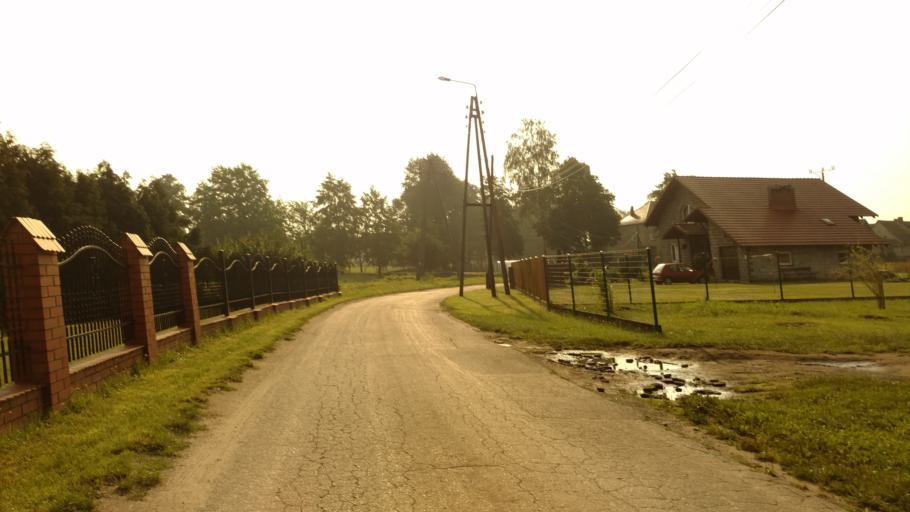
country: PL
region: Silesian Voivodeship
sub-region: Powiat pszczynski
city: Jankowice
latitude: 50.0245
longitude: 18.9768
